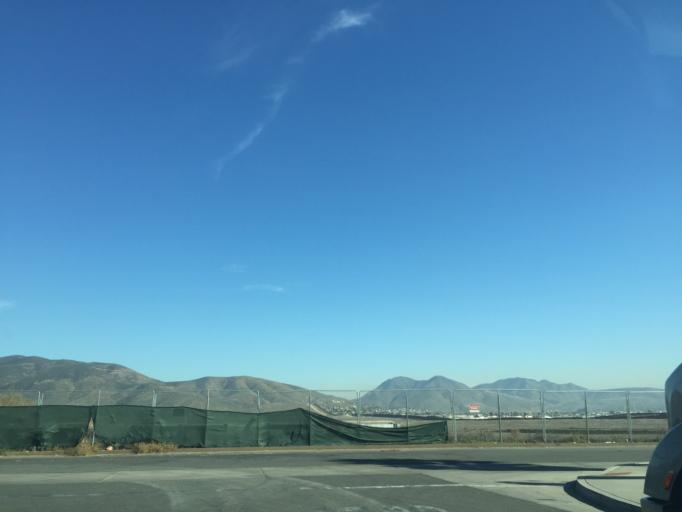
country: MX
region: Baja California
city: Tijuana
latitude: 32.5585
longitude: -116.9237
